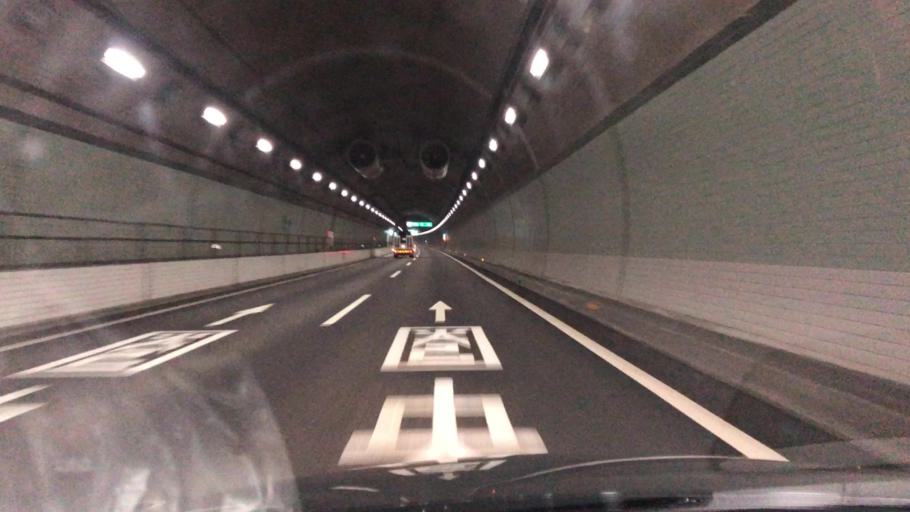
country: JP
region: Tokyo
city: Itsukaichi
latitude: 35.6632
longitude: 139.2500
